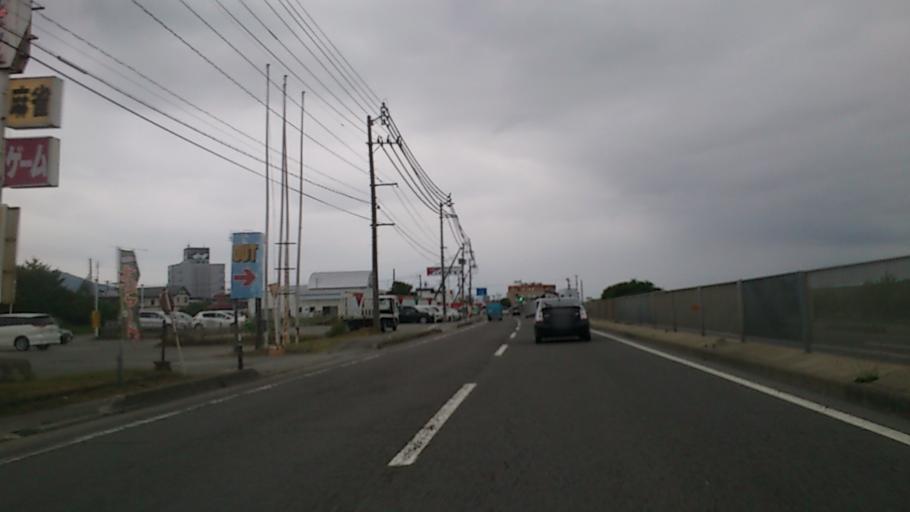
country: JP
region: Yamagata
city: Higashine
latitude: 38.4066
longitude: 140.3736
